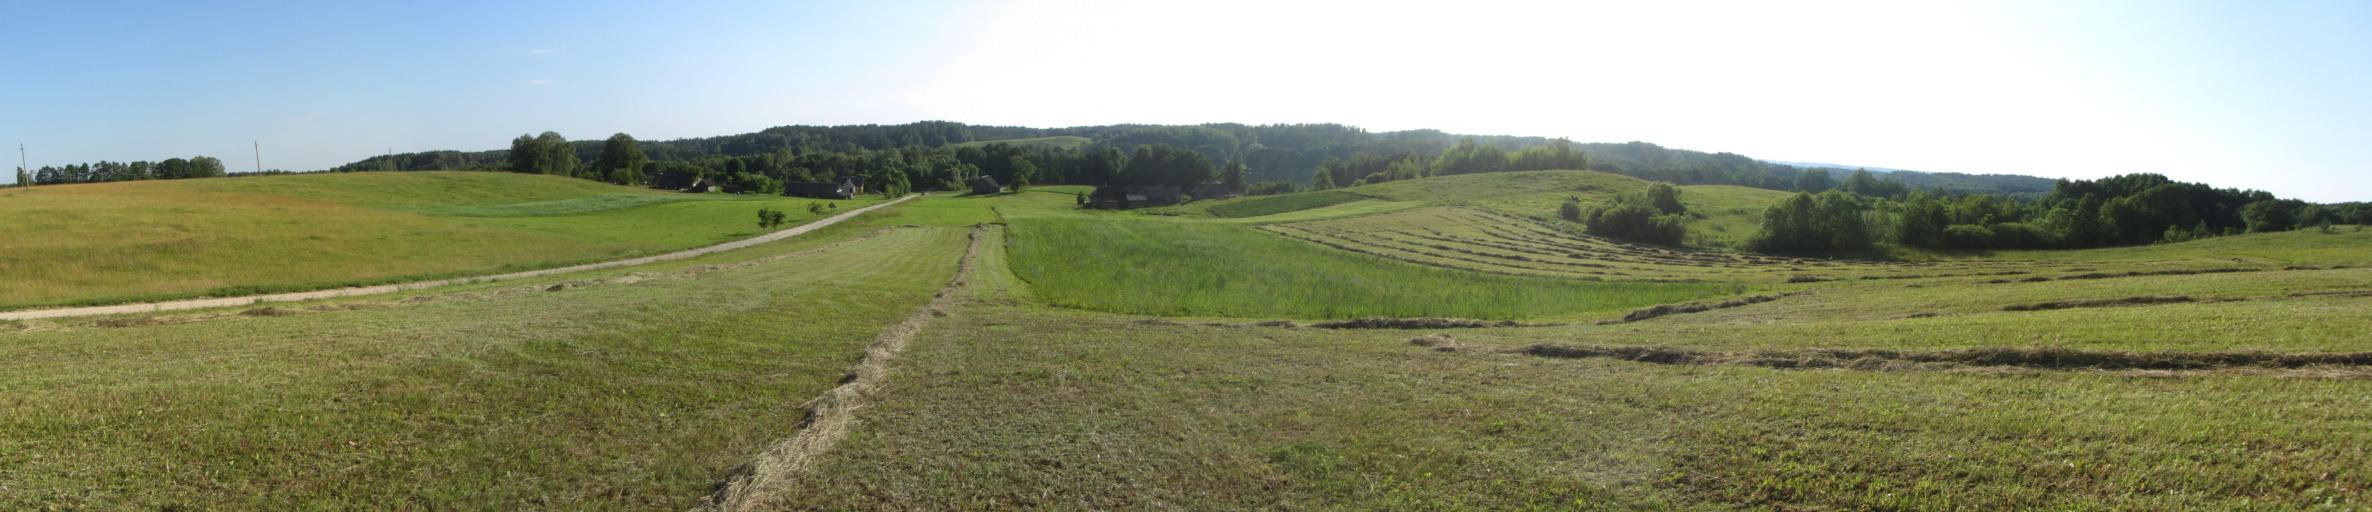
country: LT
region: Alytaus apskritis
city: Druskininkai
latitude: 54.1992
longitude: 23.9935
